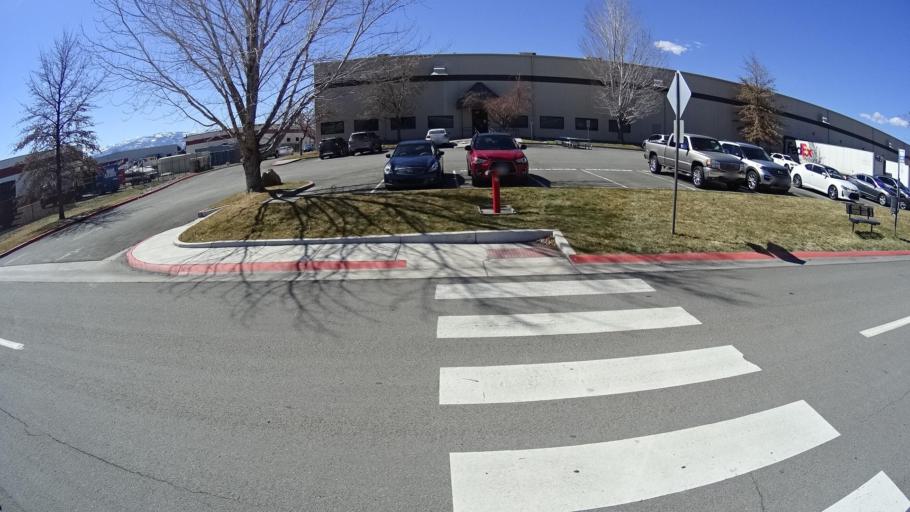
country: US
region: Nevada
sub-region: Washoe County
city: Sparks
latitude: 39.5356
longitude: -119.7113
